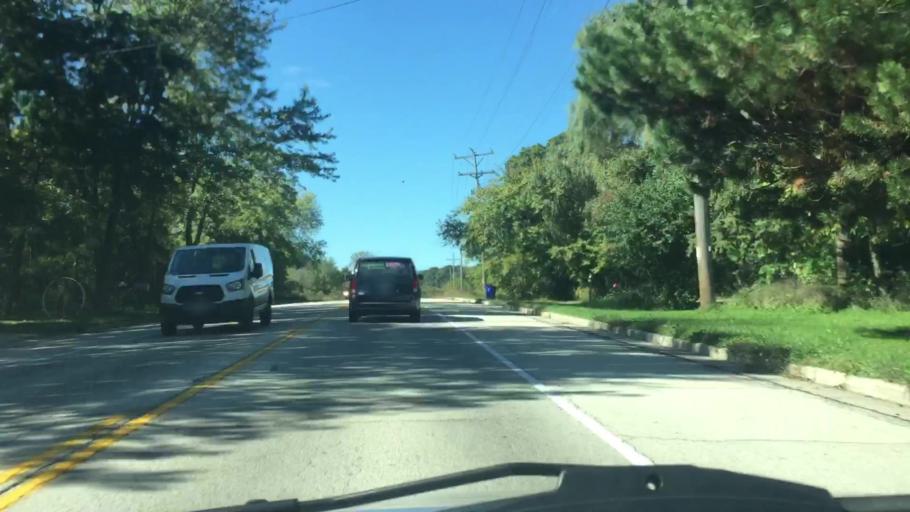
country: US
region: Wisconsin
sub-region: Waukesha County
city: Wales
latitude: 43.0197
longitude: -88.3138
